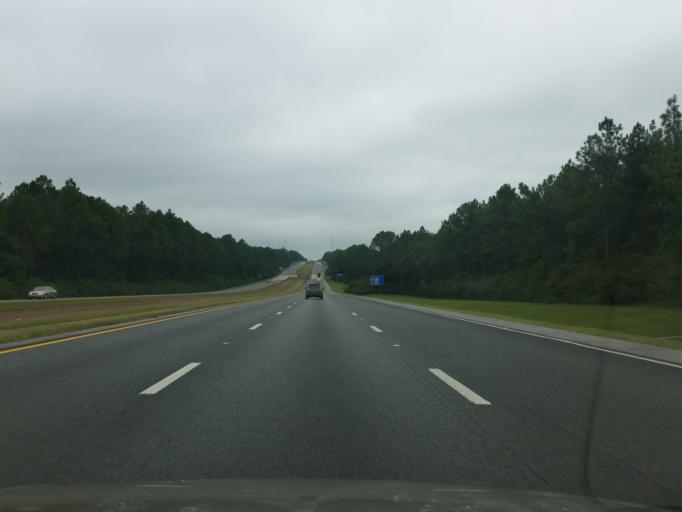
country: US
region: Florida
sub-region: Escambia County
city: Gonzalez
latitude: 30.5415
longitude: -87.3450
